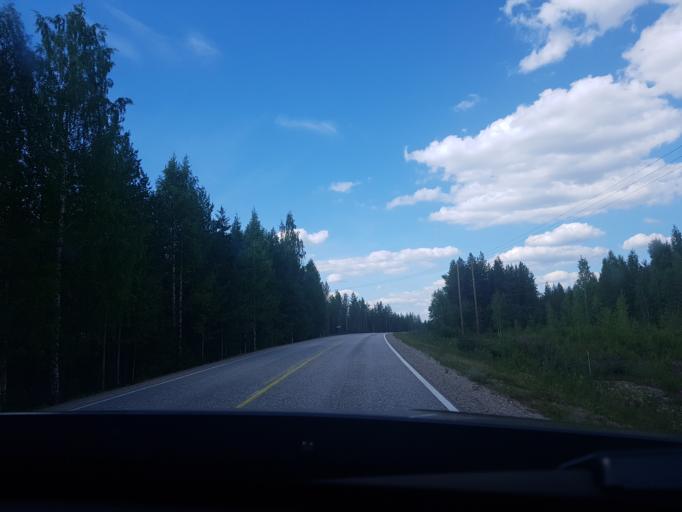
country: FI
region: Kainuu
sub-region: Kehys-Kainuu
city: Kuhmo
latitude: 64.2433
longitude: 29.8095
